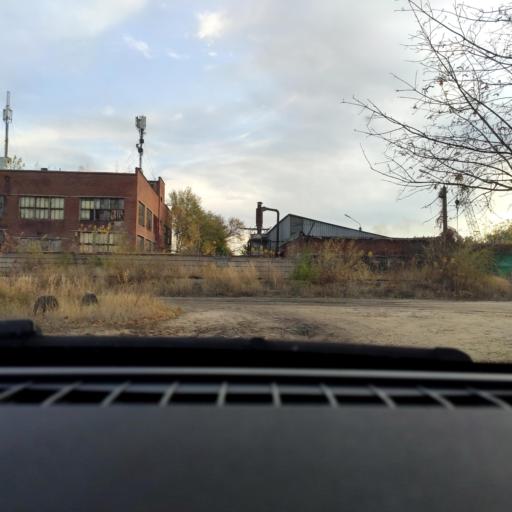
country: RU
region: Voronezj
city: Maslovka
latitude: 51.6065
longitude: 39.2330
